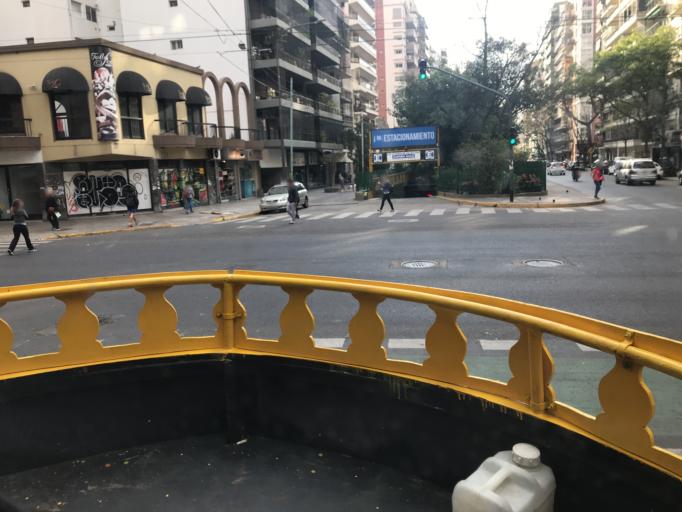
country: AR
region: Buenos Aires F.D.
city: Retiro
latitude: -34.5918
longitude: -58.4123
